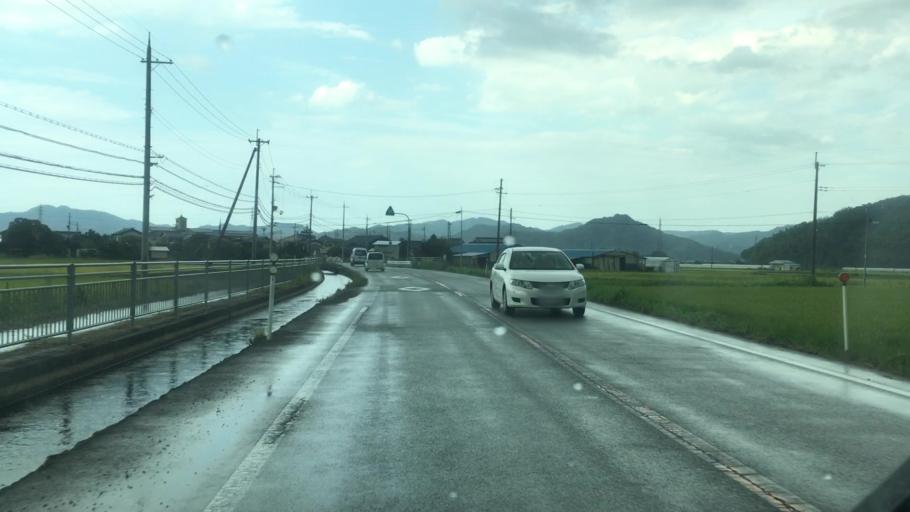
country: JP
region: Hyogo
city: Toyooka
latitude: 35.4982
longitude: 134.8175
